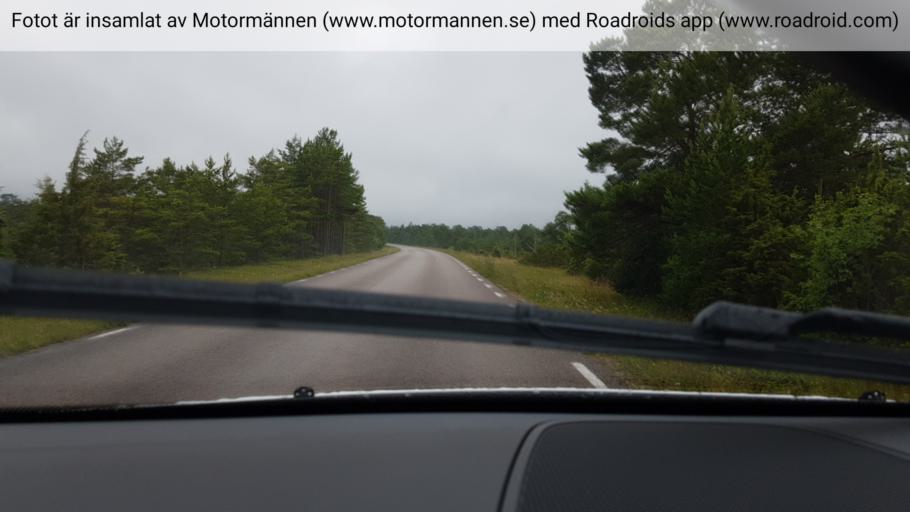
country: SE
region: Gotland
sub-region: Gotland
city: Slite
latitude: 57.9105
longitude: 18.9235
